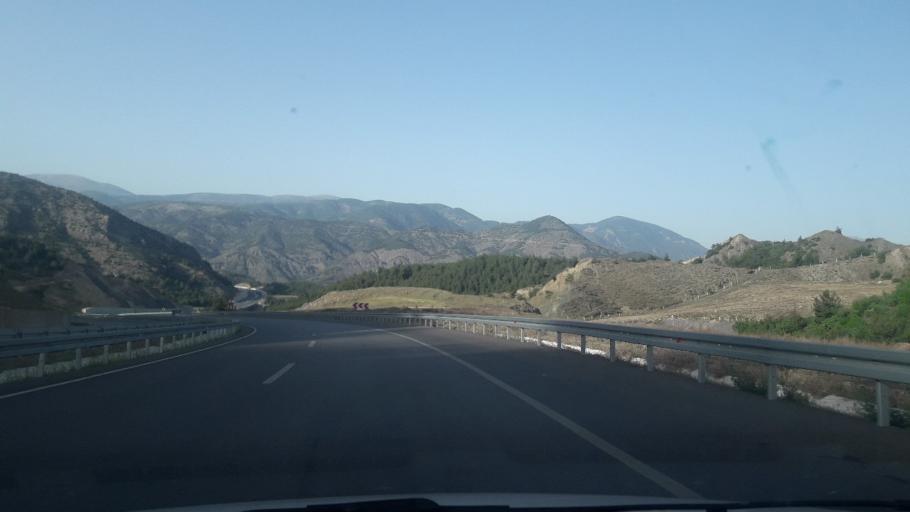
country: TR
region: Amasya
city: Amasya
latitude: 40.6718
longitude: 35.8022
